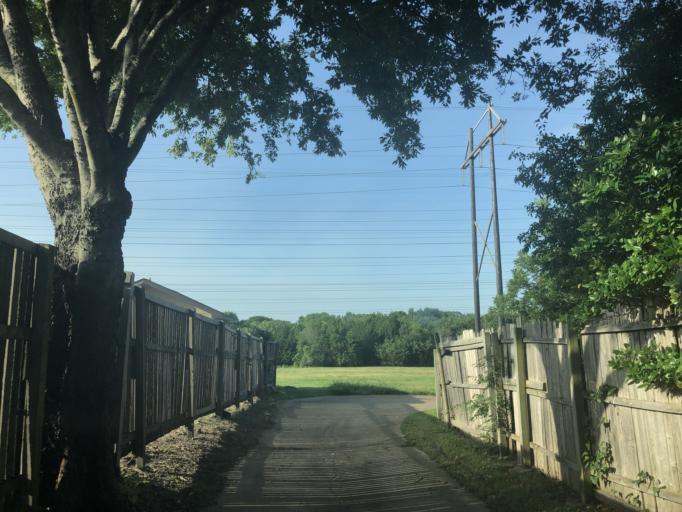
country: US
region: Texas
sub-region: Dallas County
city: Sunnyvale
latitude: 32.8346
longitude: -96.5873
